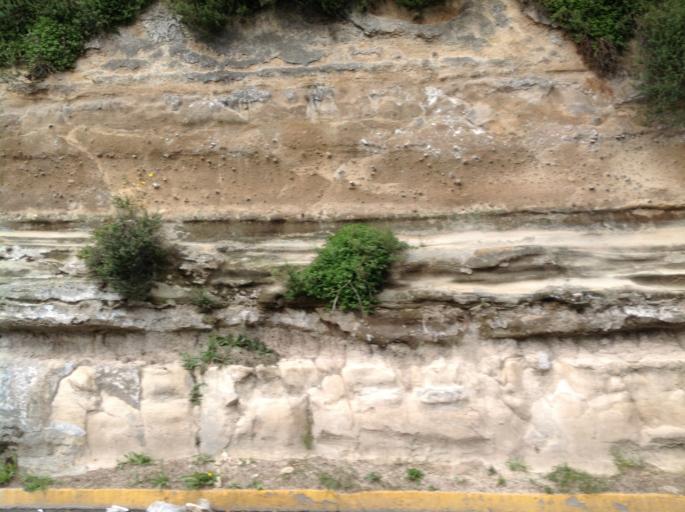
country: MX
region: Mexico
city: Ciudad Lopez Mateos
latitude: 19.6048
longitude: -99.2264
